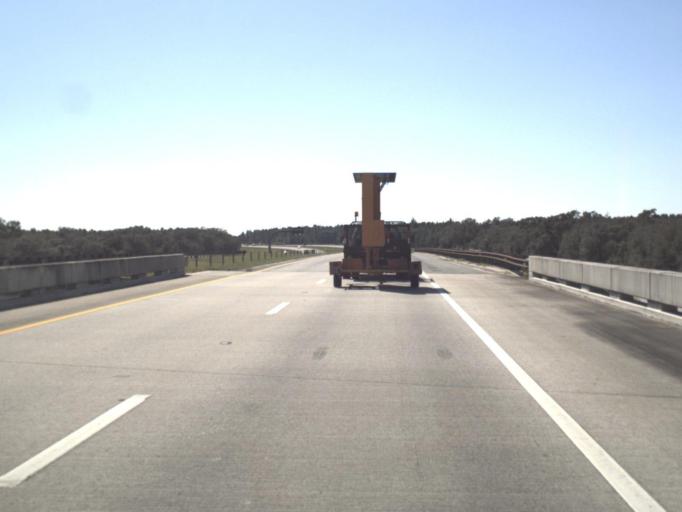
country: US
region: Florida
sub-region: Pasco County
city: Shady Hills
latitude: 28.3720
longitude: -82.5435
